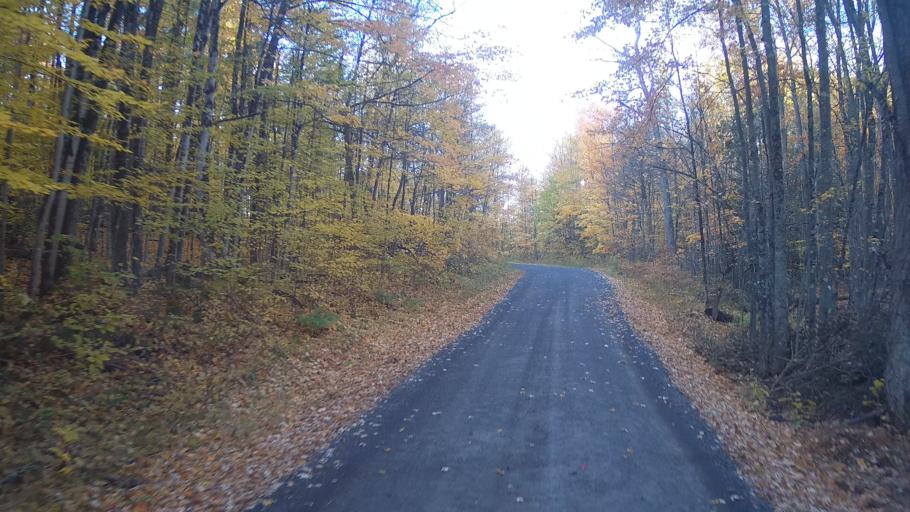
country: CA
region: Ontario
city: Arnprior
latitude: 45.3322
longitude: -76.3662
